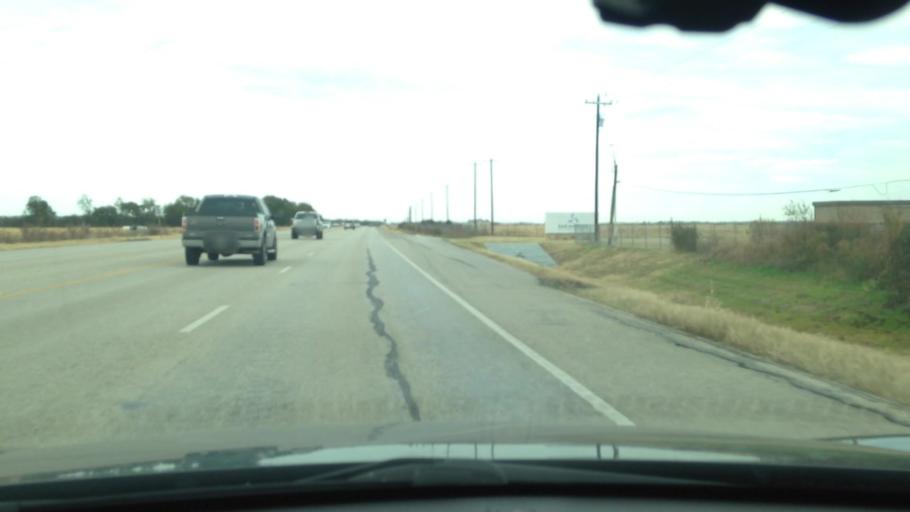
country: US
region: Texas
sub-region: Hays County
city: San Marcos
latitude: 29.8939
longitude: -97.8804
